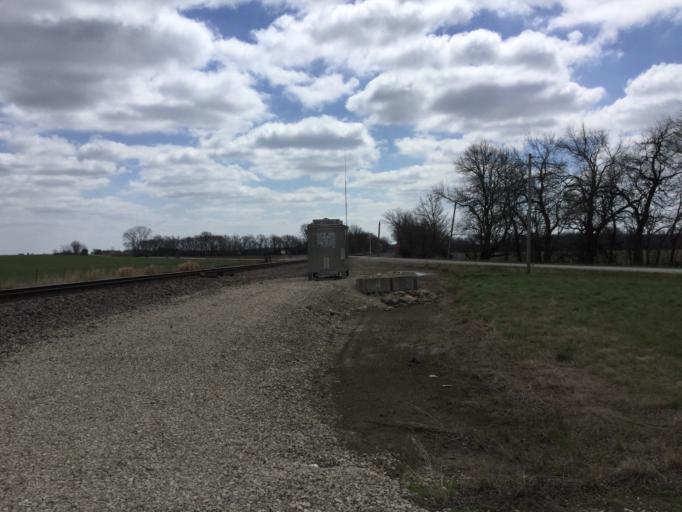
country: US
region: Kansas
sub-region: Bourbon County
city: Fort Scott
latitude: 37.7461
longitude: -94.6392
